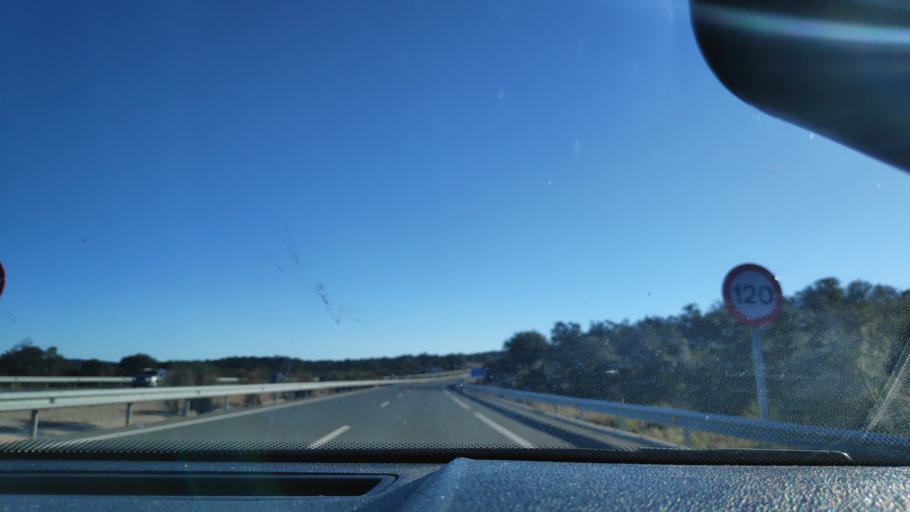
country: ES
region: Andalusia
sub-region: Provincia de Huelva
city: Santa Olalla del Cala
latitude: 37.9420
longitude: -6.2275
